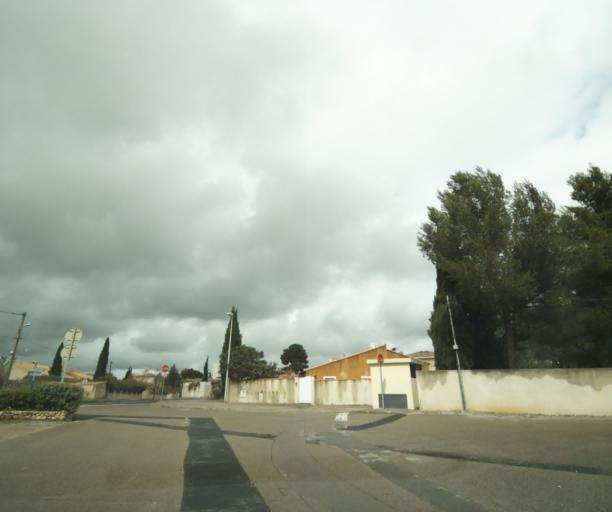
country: FR
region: Languedoc-Roussillon
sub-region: Departement de l'Herault
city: Cournonsec
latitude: 43.5525
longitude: 3.7101
